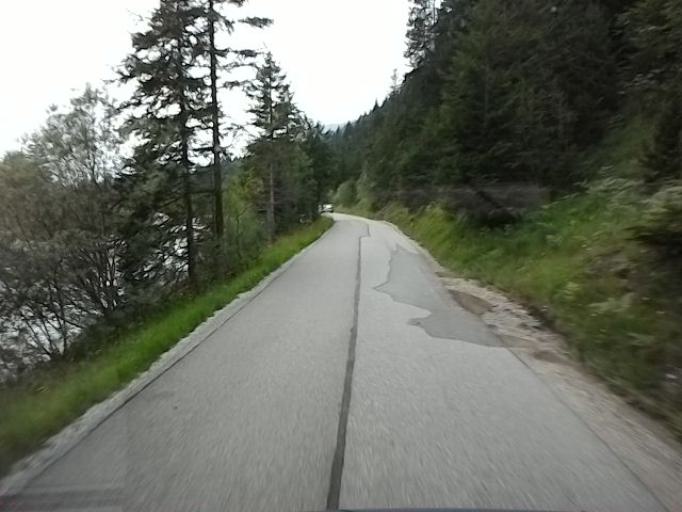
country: DE
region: Bavaria
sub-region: Upper Bavaria
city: Jachenau
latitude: 47.5508
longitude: 11.3917
